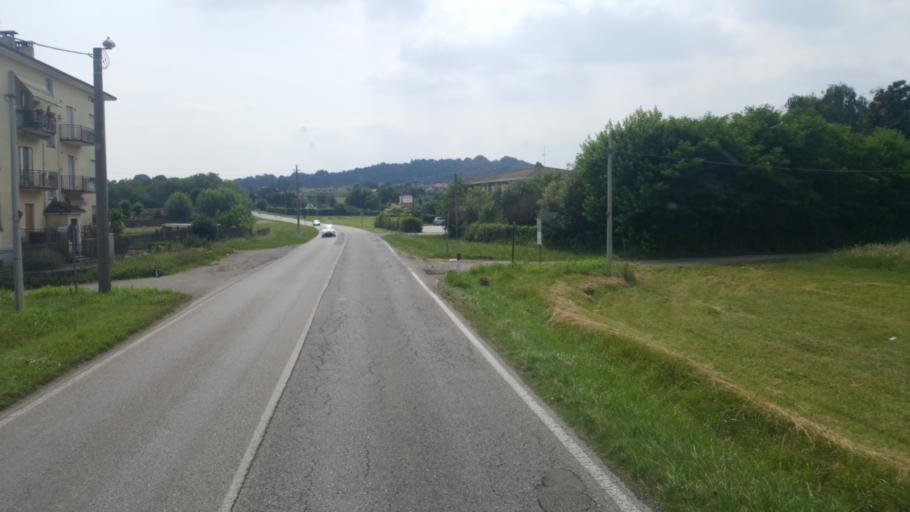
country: IT
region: Lombardy
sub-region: Provincia di Como
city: Lurate Caccivio
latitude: 45.7569
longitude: 8.9927
